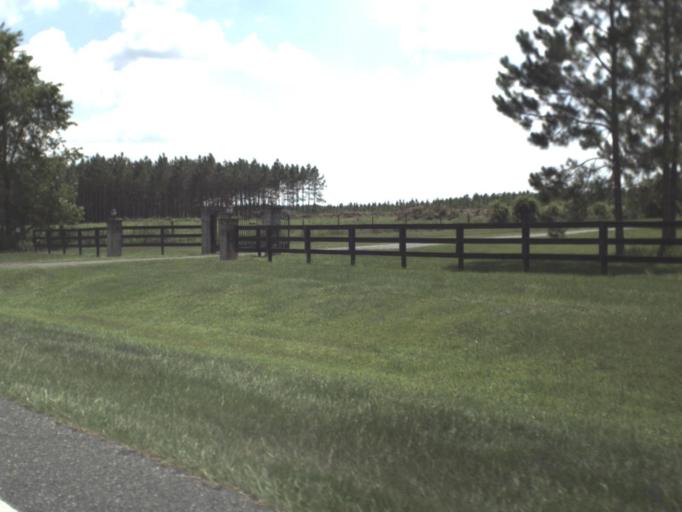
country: US
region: Florida
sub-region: Alachua County
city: High Springs
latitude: 29.9163
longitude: -82.6094
